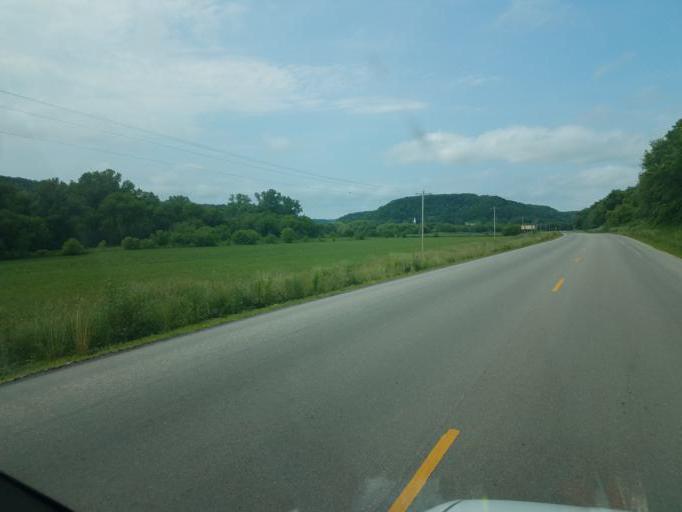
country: US
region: Wisconsin
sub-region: Monroe County
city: Cashton
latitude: 43.7300
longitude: -90.6529
